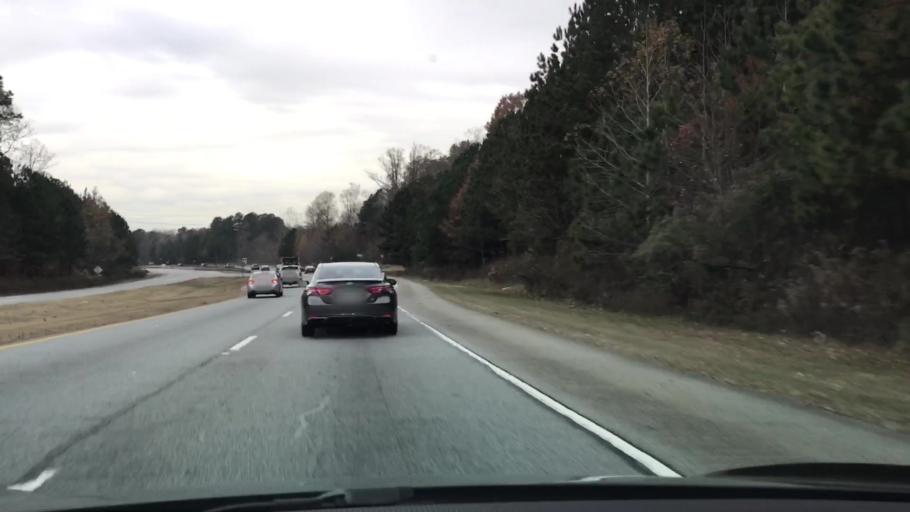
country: US
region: Georgia
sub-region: Gwinnett County
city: Suwanee
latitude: 34.0351
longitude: -84.1047
